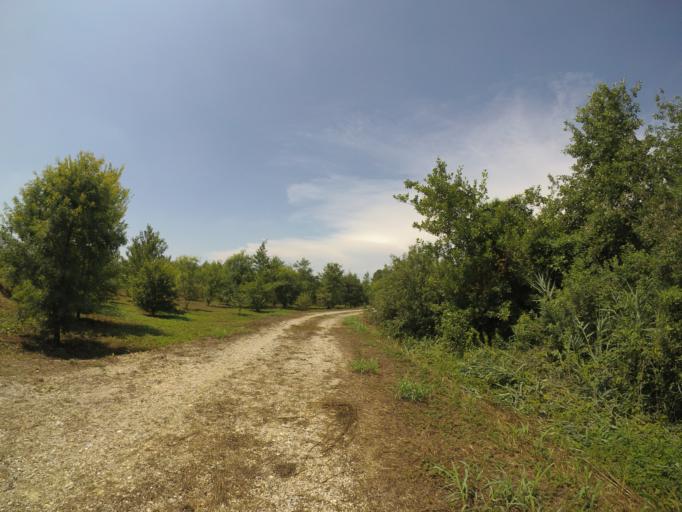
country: IT
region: Friuli Venezia Giulia
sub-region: Provincia di Udine
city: Rivignano
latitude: 45.8982
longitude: 13.0713
